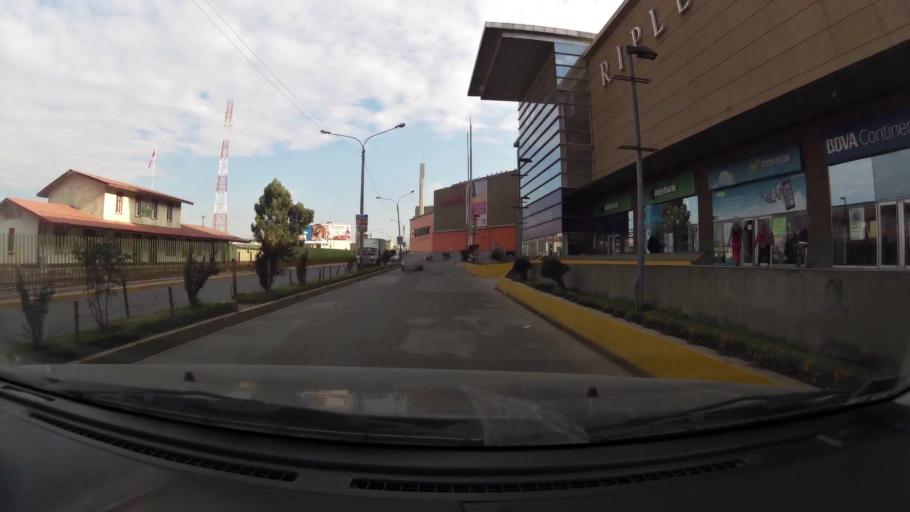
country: PE
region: Junin
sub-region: Provincia de Huancayo
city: Huancayo
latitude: -12.0677
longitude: -75.2054
